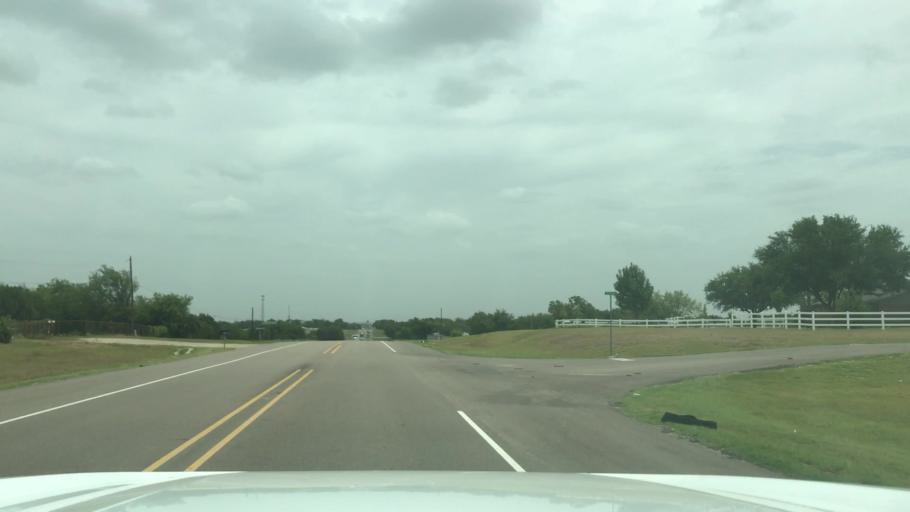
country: US
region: Texas
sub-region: McLennan County
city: Woodway
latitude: 31.5881
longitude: -97.3236
